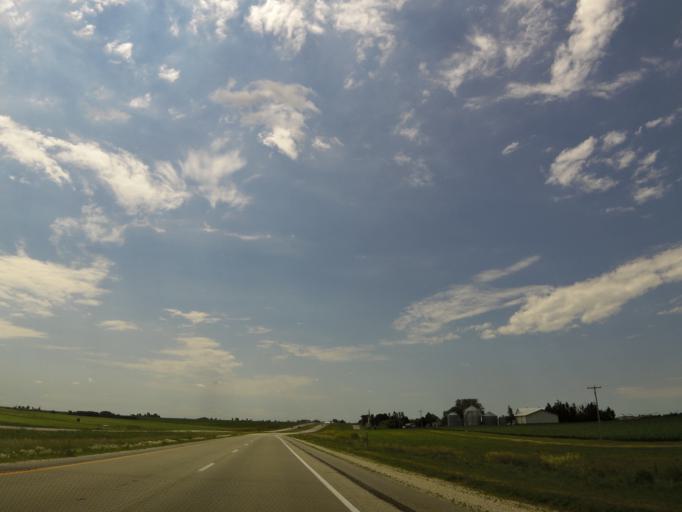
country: US
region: Iowa
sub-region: Bremer County
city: Tripoli
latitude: 42.7627
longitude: -92.3370
